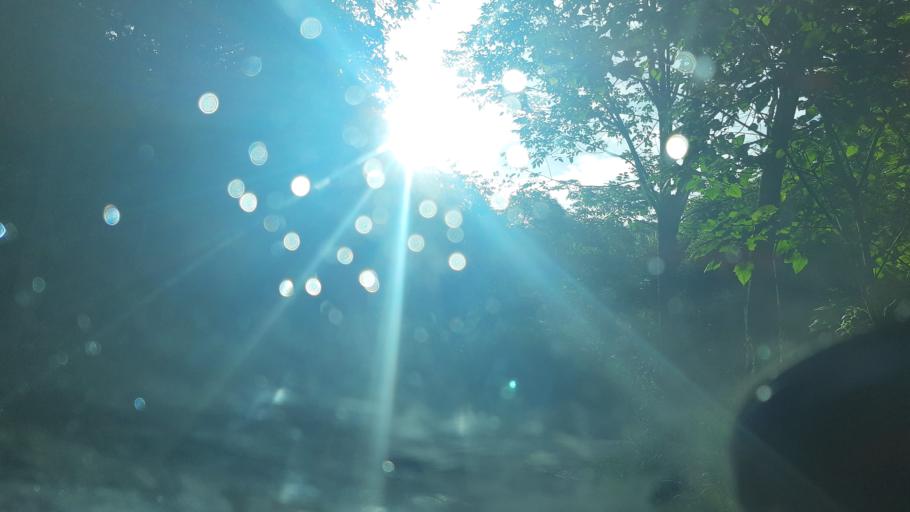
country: CO
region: Cundinamarca
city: Tenza
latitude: 5.0745
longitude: -73.4112
